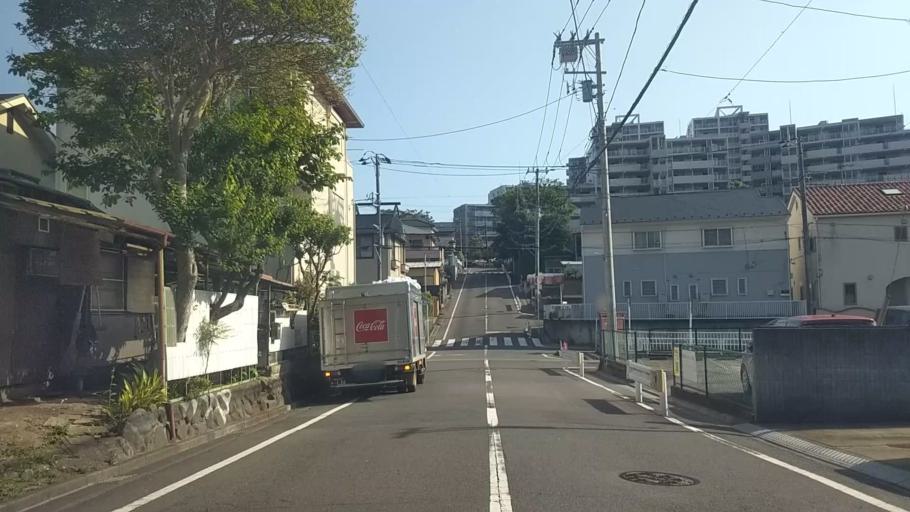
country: JP
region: Kanagawa
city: Fujisawa
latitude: 35.3463
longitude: 139.4904
